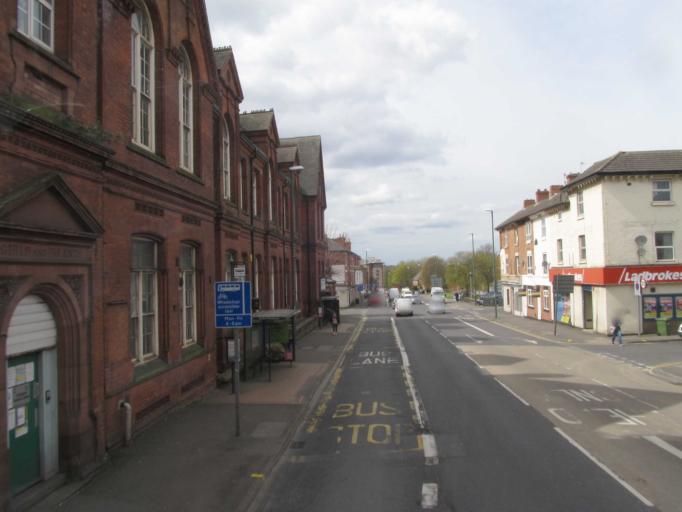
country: GB
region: England
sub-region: Nottingham
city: Nottingham
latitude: 52.9556
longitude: -1.1760
